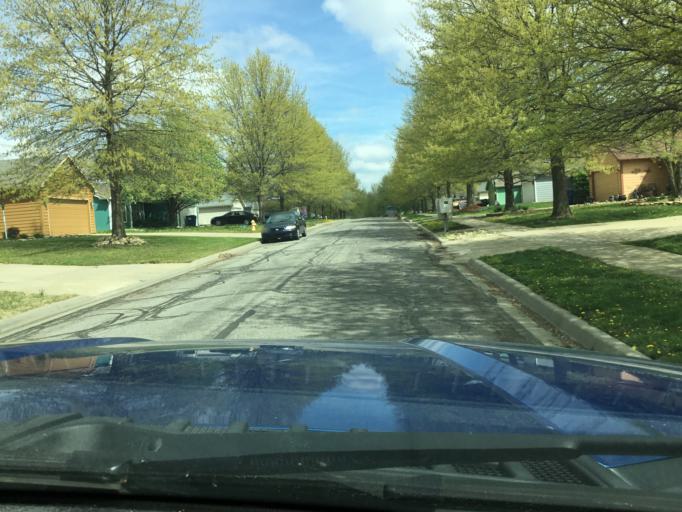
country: US
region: Kansas
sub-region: Douglas County
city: Lawrence
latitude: 38.9362
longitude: -95.2100
